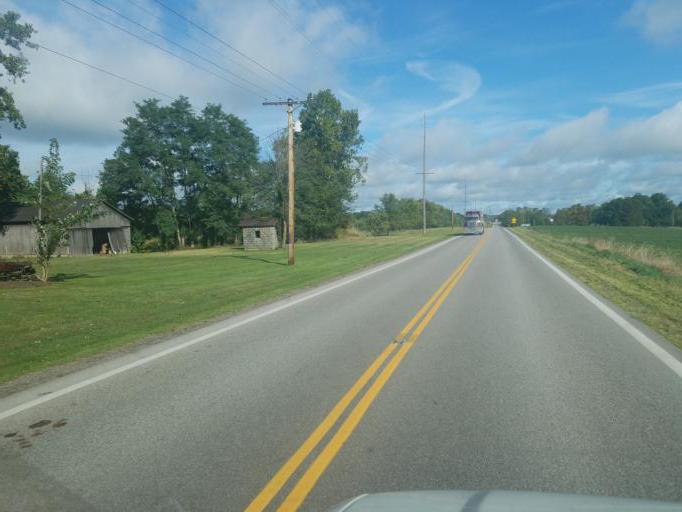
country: US
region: Ohio
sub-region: Wayne County
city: West Salem
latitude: 41.0029
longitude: -82.1148
